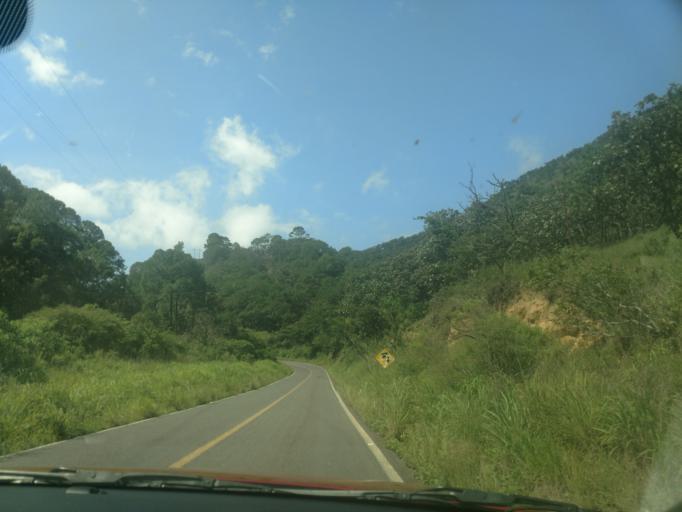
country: MX
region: Jalisco
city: Talpa de Allende
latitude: 20.4286
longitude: -104.7971
